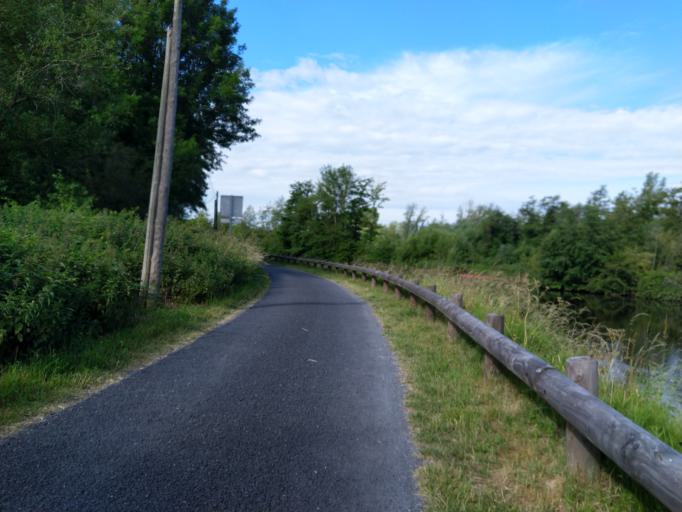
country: FR
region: Nord-Pas-de-Calais
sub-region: Departement du Nord
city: Marpent
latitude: 50.2979
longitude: 4.0814
